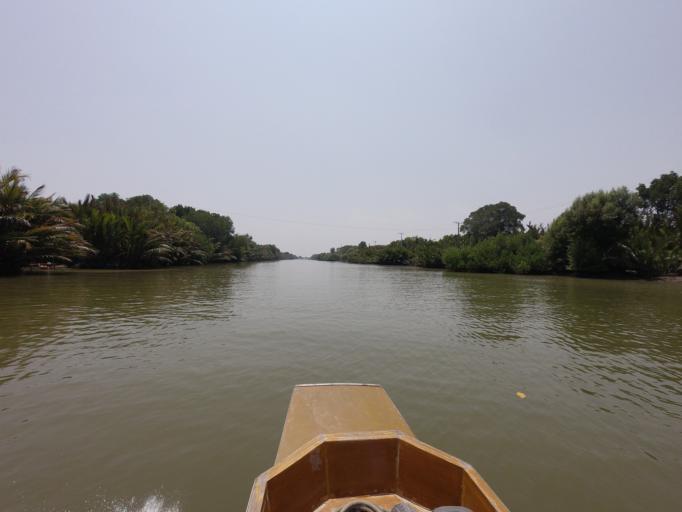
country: TH
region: Bangkok
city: Thung Khru
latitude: 13.5427
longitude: 100.4610
